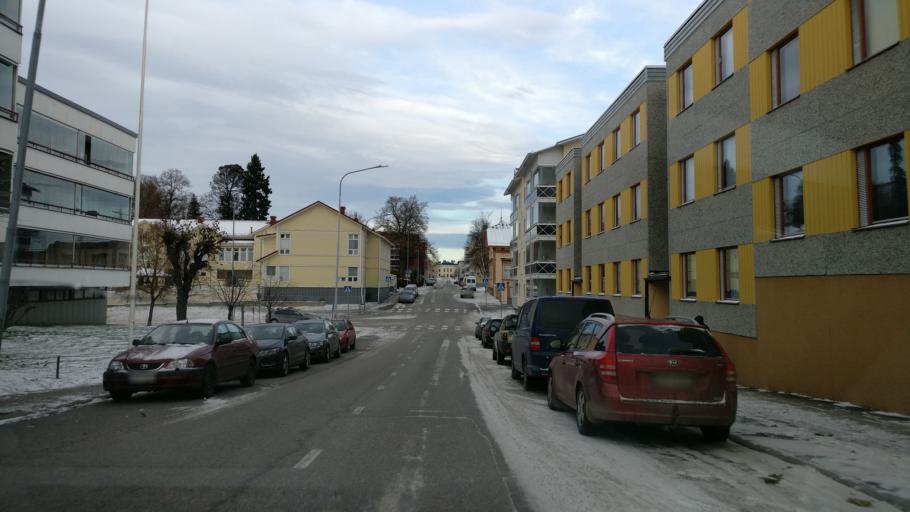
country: FI
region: Southern Savonia
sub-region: Savonlinna
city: Savonlinna
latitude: 61.8668
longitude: 28.8779
